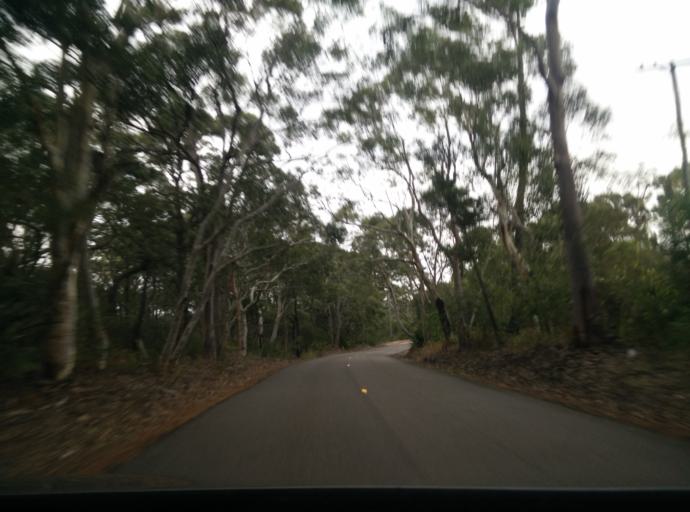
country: AU
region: New South Wales
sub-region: Gosford Shire
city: Narara
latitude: -33.3665
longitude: 151.3256
